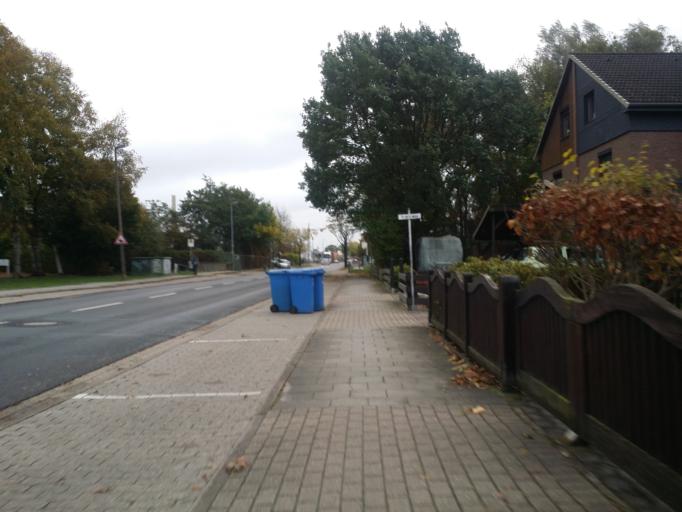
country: DE
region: Lower Saxony
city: Delmenhorst
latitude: 53.0236
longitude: 8.6388
